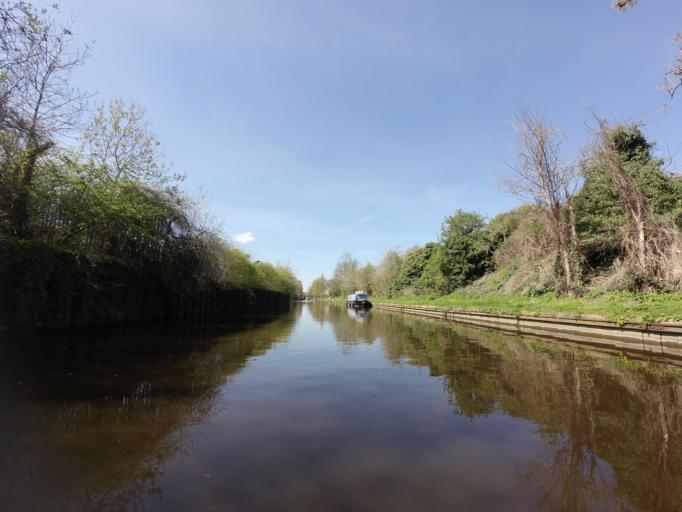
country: GB
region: England
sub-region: Greater London
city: Hayes
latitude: 51.5057
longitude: -0.4221
